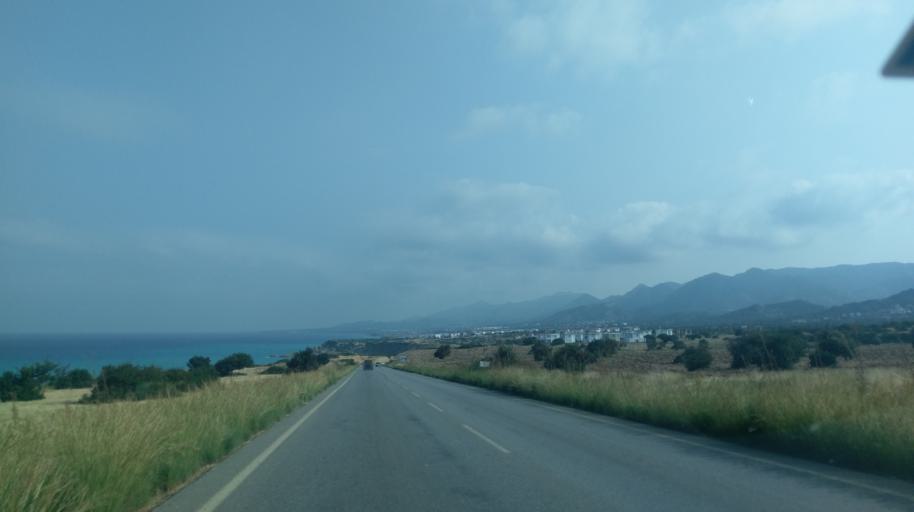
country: CY
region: Ammochostos
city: Lefkonoiko
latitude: 35.3533
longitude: 33.6085
